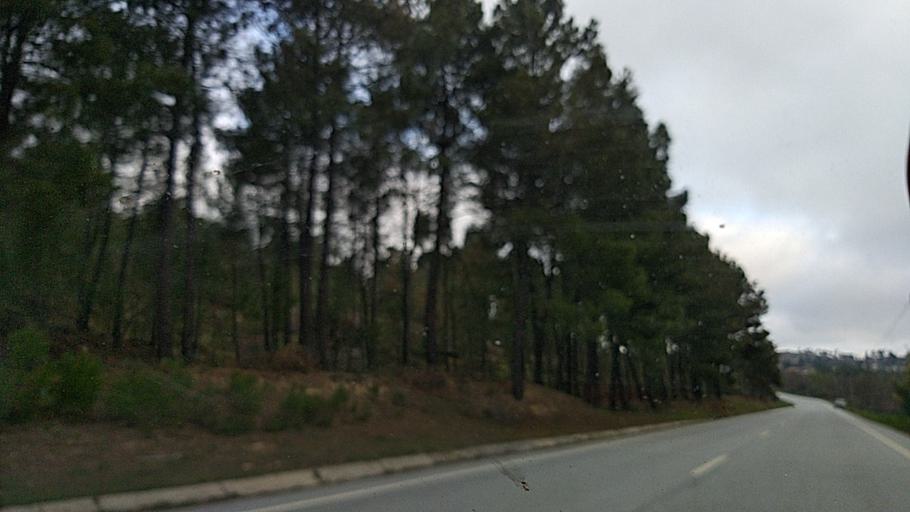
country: PT
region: Guarda
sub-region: Fornos de Algodres
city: Fornos de Algodres
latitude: 40.6475
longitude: -7.4906
